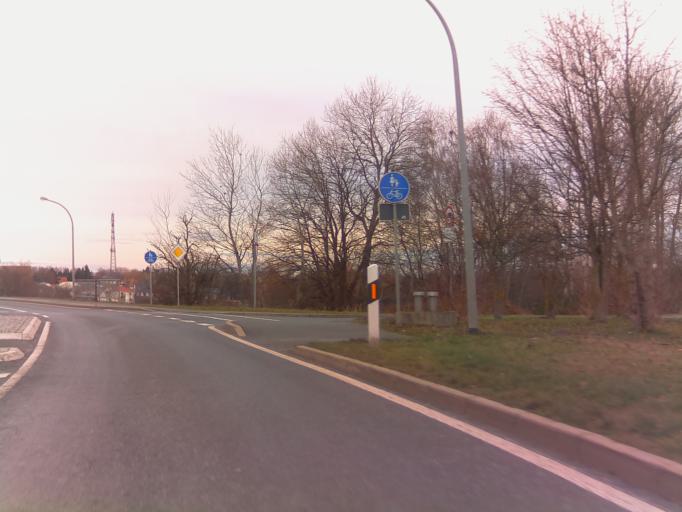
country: DE
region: Thuringia
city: Hermsdorf
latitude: 50.8835
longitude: 11.8607
